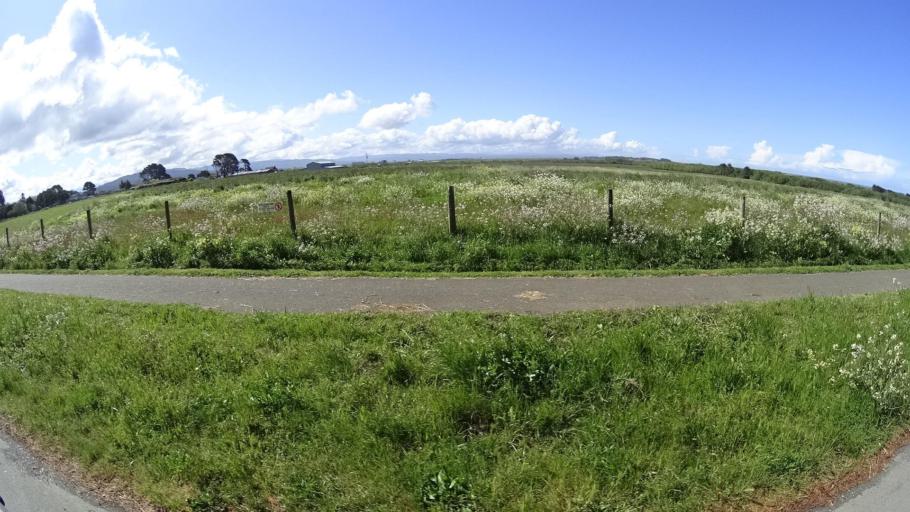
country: US
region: California
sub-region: Humboldt County
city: McKinleyville
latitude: 40.9339
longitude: -124.1228
